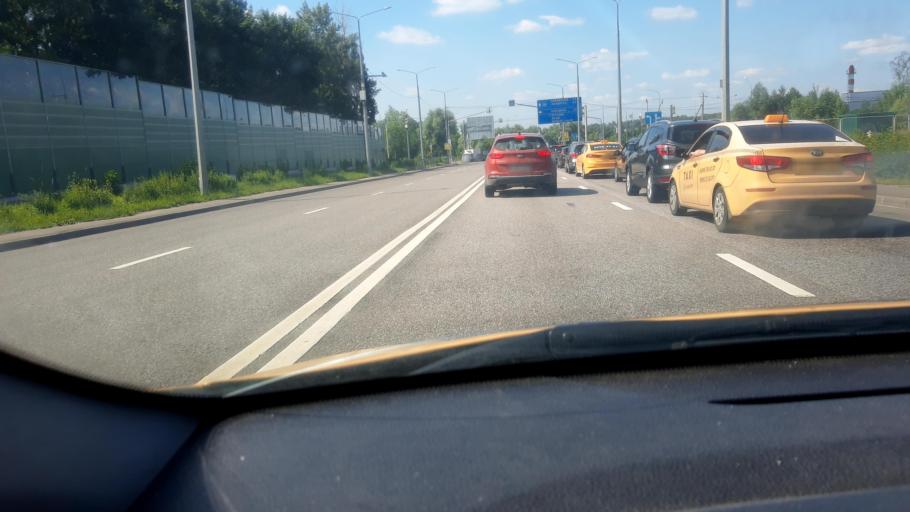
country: RU
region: Moskovskaya
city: Kokoshkino
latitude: 55.5784
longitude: 37.1642
